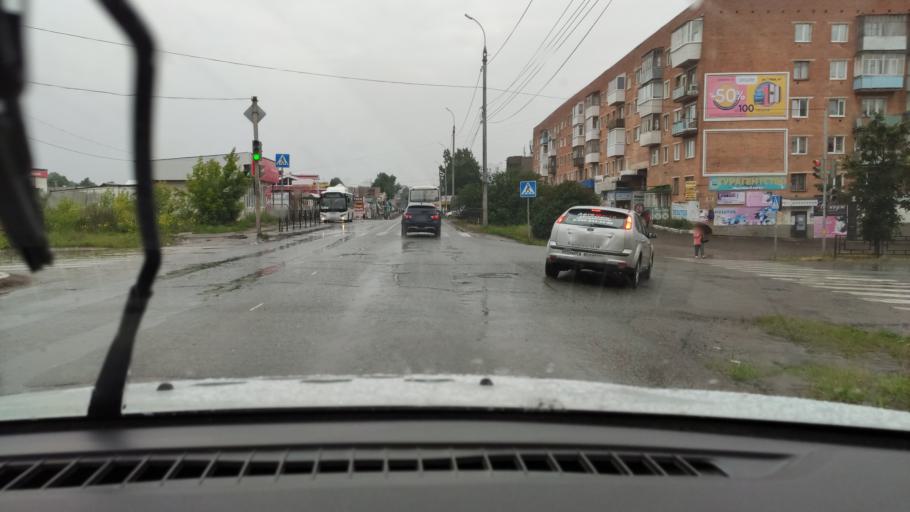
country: RU
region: Udmurtiya
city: Votkinsk
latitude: 57.0626
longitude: 53.9977
